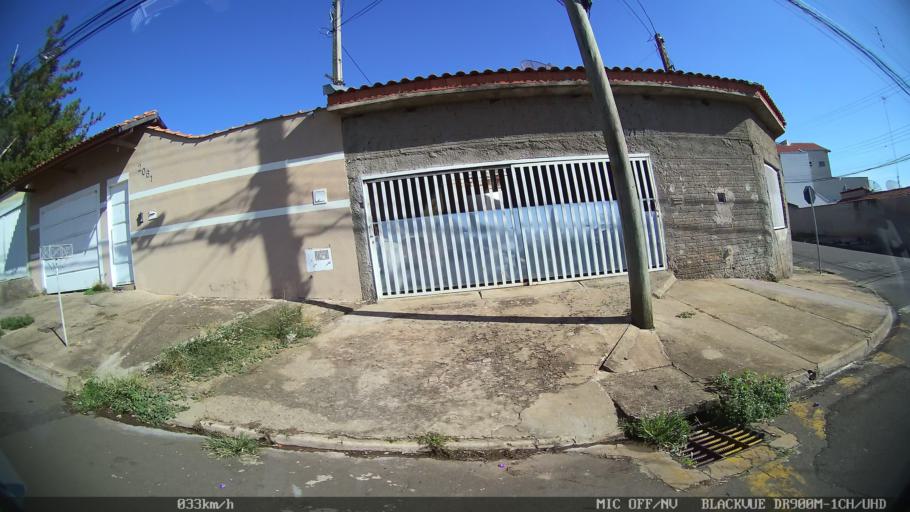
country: BR
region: Sao Paulo
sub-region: Franca
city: Franca
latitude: -20.4926
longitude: -47.4252
